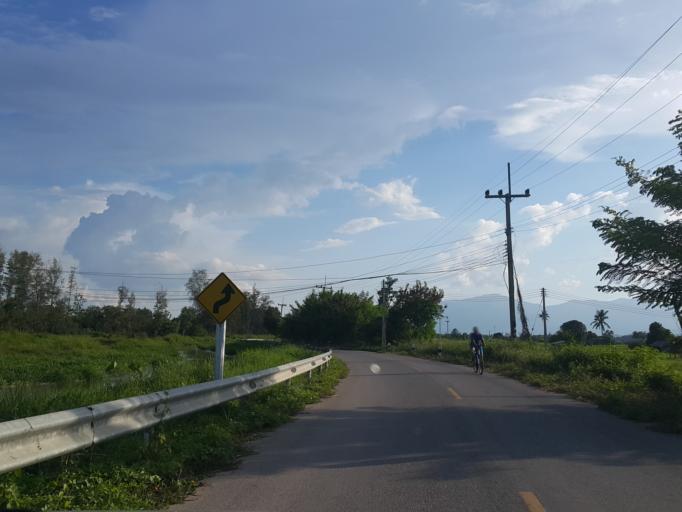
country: TH
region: Chiang Mai
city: Mae Taeng
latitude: 19.0168
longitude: 98.9854
